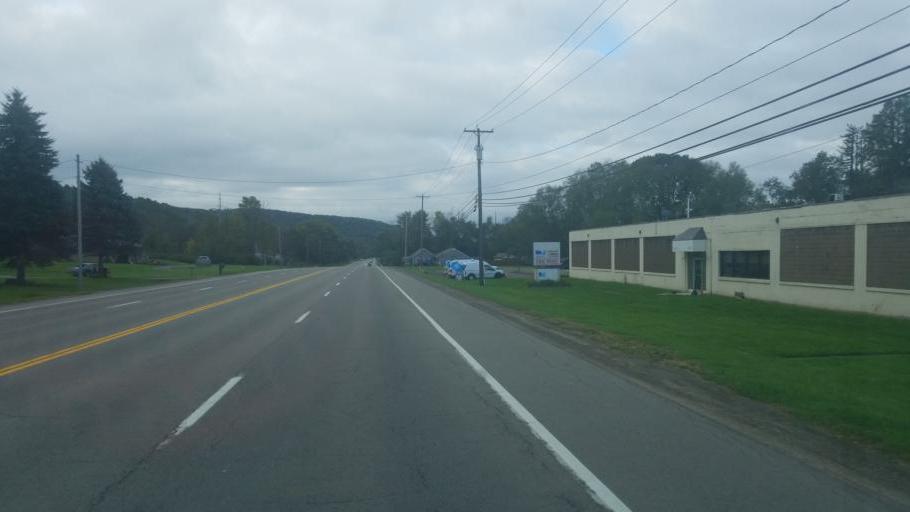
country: US
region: New York
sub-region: Cattaraugus County
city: Olean
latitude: 42.1483
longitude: -78.3992
